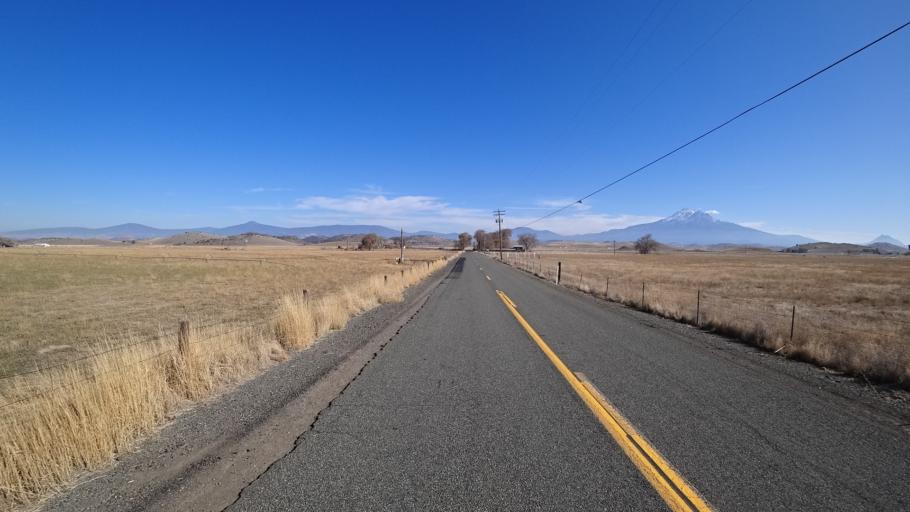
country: US
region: California
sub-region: Siskiyou County
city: Montague
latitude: 41.5746
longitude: -122.5308
